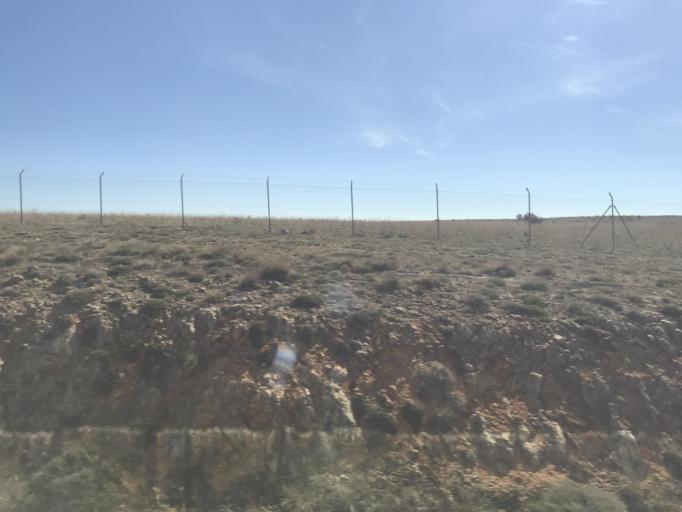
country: ES
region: Castille-La Mancha
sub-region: Provincia de Guadalajara
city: Anguita
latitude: 41.1141
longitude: -2.3581
